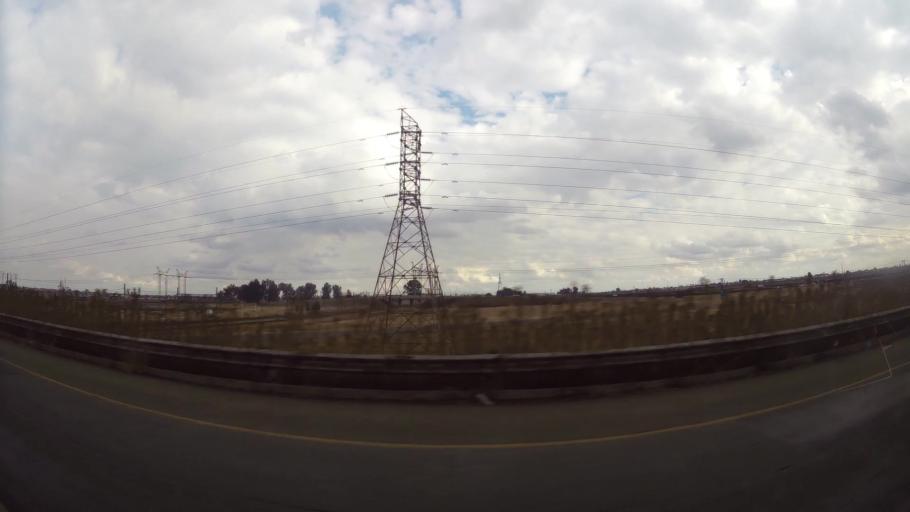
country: ZA
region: Orange Free State
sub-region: Fezile Dabi District Municipality
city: Sasolburg
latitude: -26.8390
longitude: 27.8736
